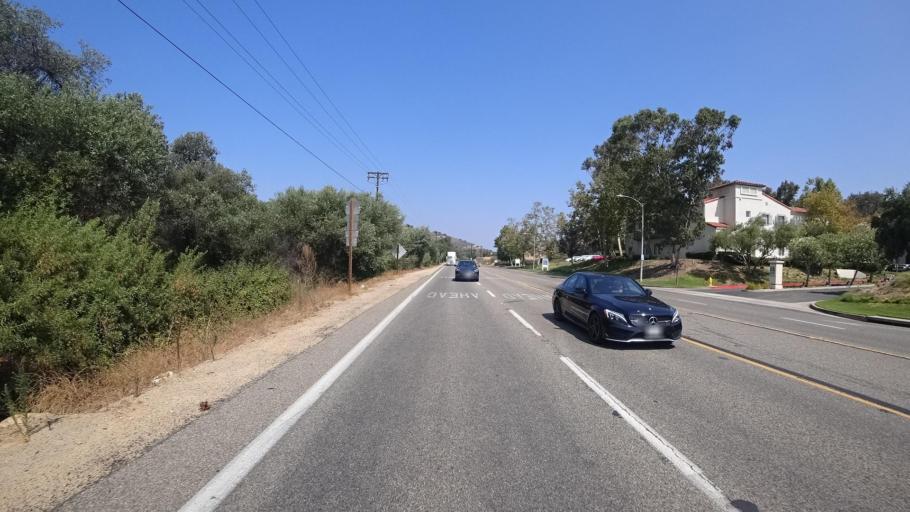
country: US
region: California
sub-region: San Diego County
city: Bonsall
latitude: 33.2959
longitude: -117.2236
